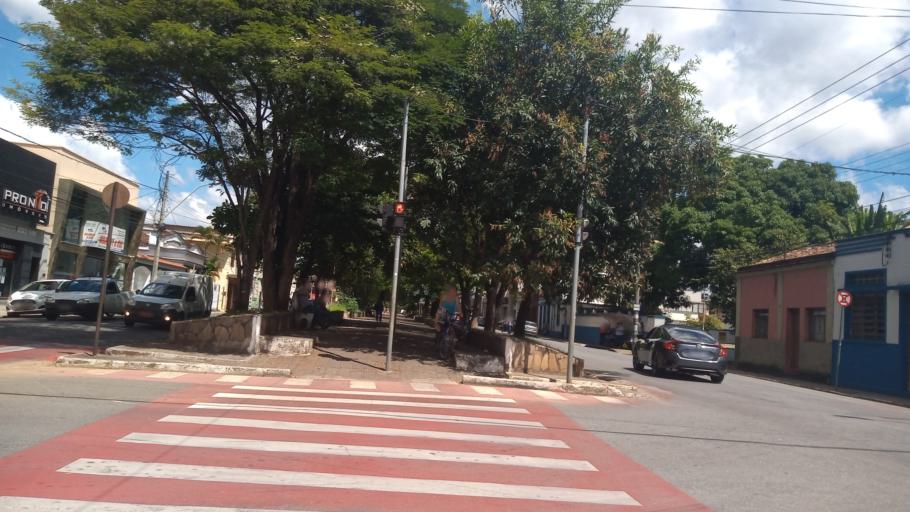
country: BR
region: Minas Gerais
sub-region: Sao Joao Del Rei
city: Sao Joao del Rei
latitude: -21.1251
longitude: -44.2483
